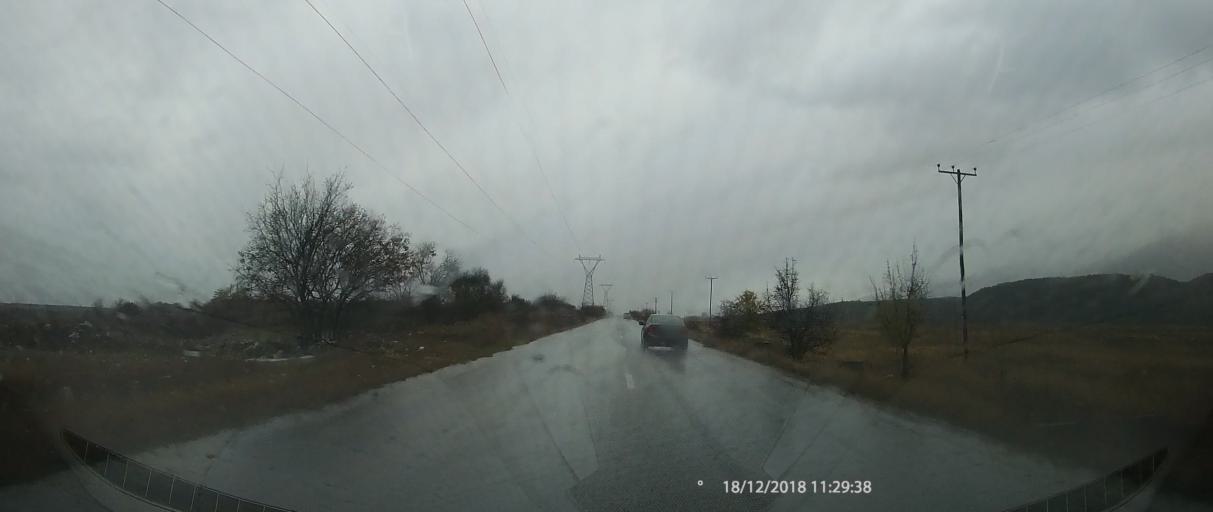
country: GR
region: Central Macedonia
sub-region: Nomos Pierias
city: Litochoro
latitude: 40.1334
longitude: 22.5215
